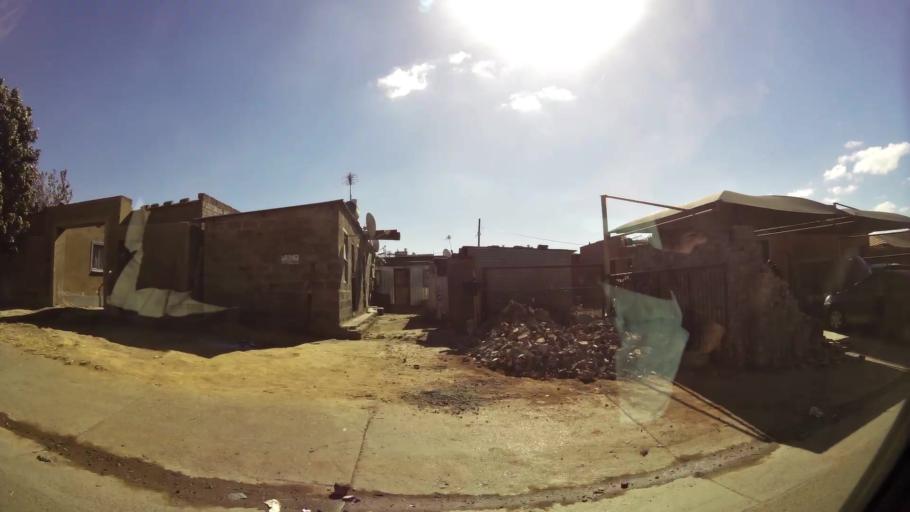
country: ZA
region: Gauteng
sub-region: City of Johannesburg Metropolitan Municipality
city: Modderfontein
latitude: -26.0356
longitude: 28.1837
